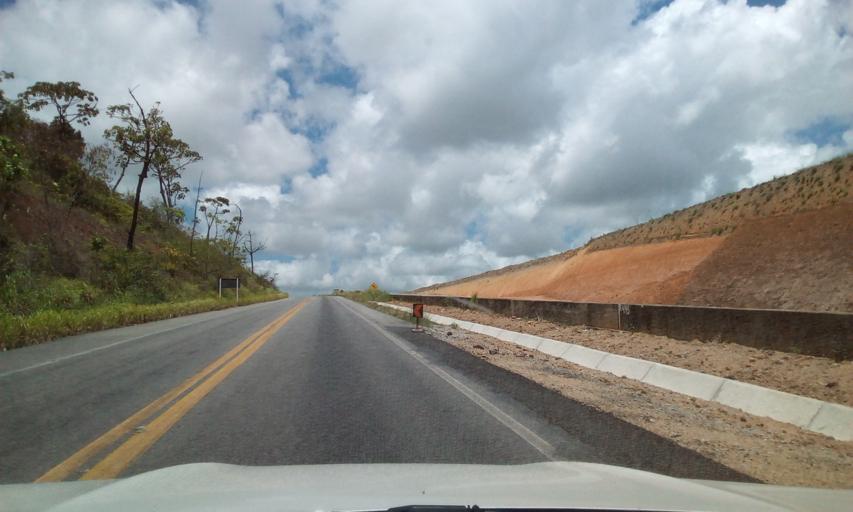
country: BR
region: Alagoas
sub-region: Sao Miguel Dos Campos
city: Sao Miguel dos Campos
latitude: -9.8841
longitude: -36.1381
